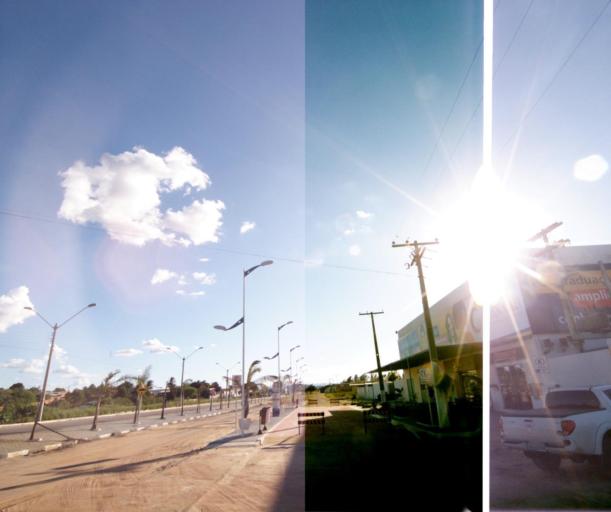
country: BR
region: Bahia
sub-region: Guanambi
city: Guanambi
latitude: -14.2046
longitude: -42.7599
